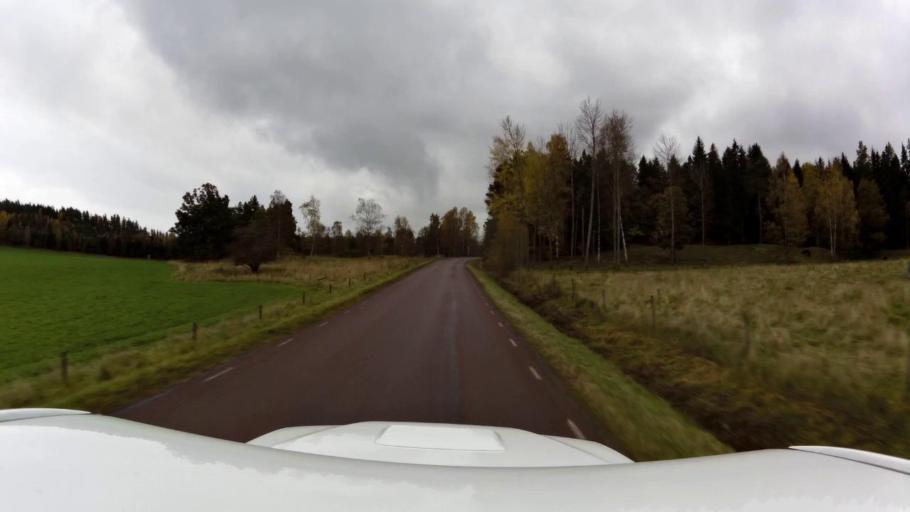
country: SE
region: OEstergoetland
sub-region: Linkopings Kommun
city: Ljungsbro
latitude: 58.5405
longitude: 15.5255
